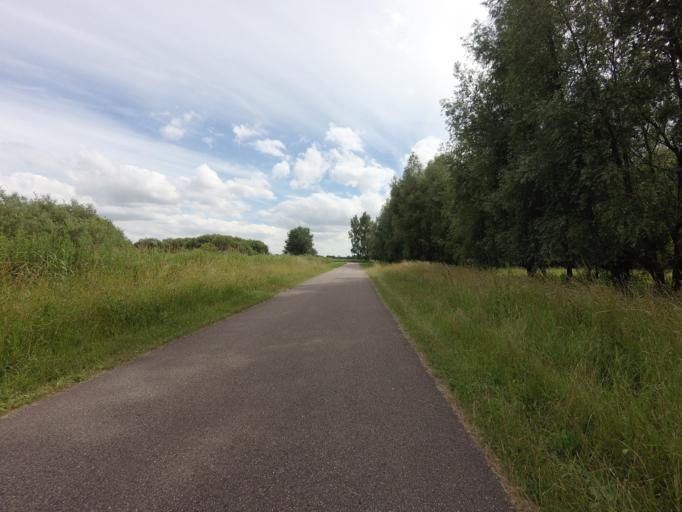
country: NL
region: North Holland
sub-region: Gemeente Landsmeer
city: Landsmeer
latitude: 52.4486
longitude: 4.8974
